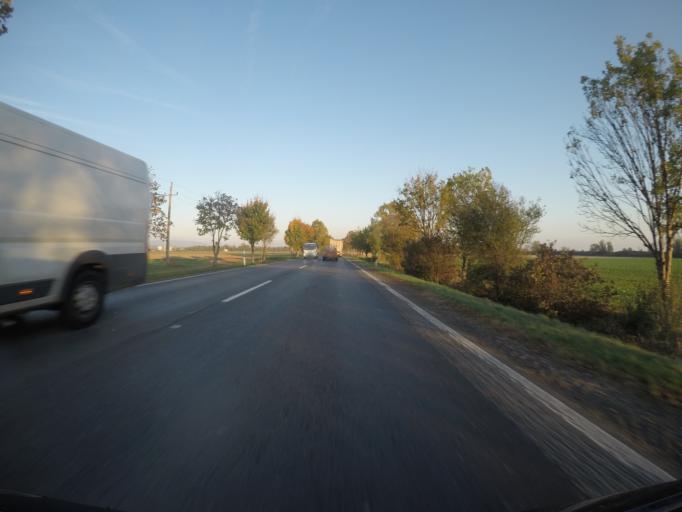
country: HU
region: Baranya
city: Szentlorinc
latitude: 46.0385
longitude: 17.9394
